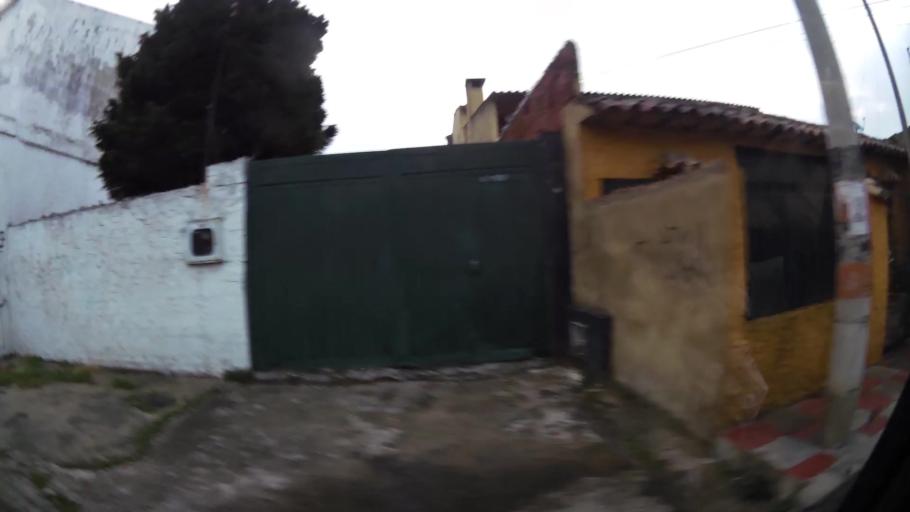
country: CO
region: Cundinamarca
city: Chia
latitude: 4.8578
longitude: -74.0567
